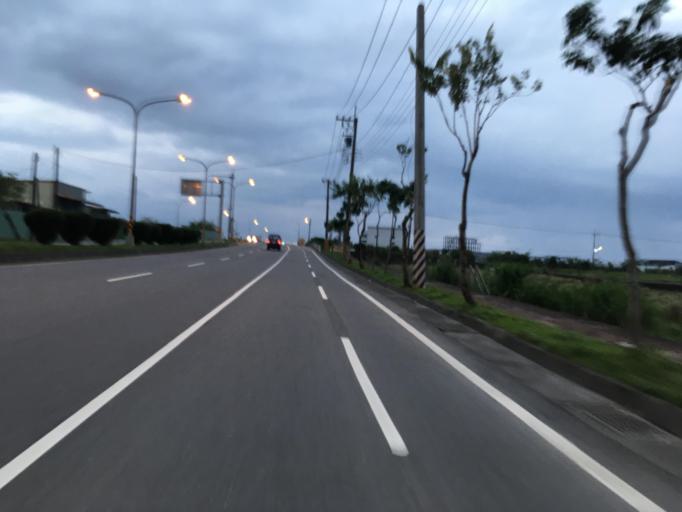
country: TW
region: Taiwan
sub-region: Yilan
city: Yilan
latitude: 24.6295
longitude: 121.8321
